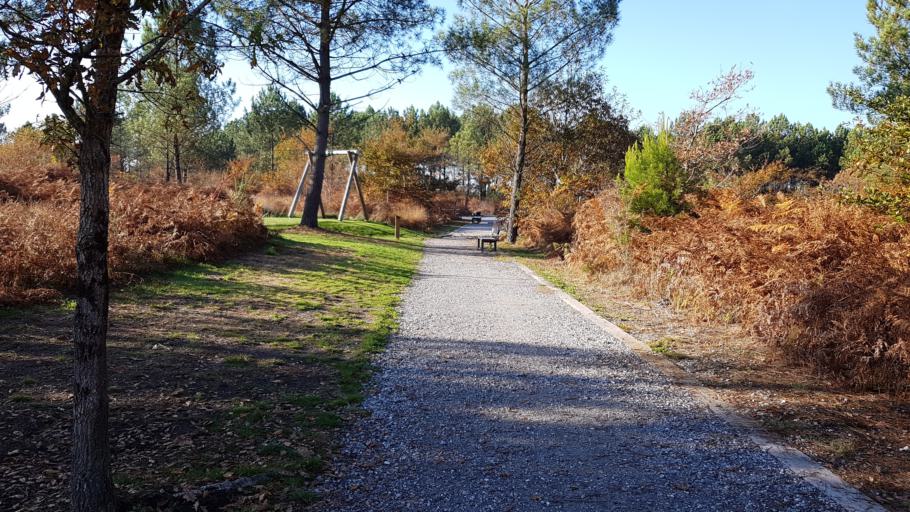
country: FR
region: Aquitaine
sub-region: Departement des Landes
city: Saint-Paul-les-Dax
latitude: 43.7363
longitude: -1.0855
